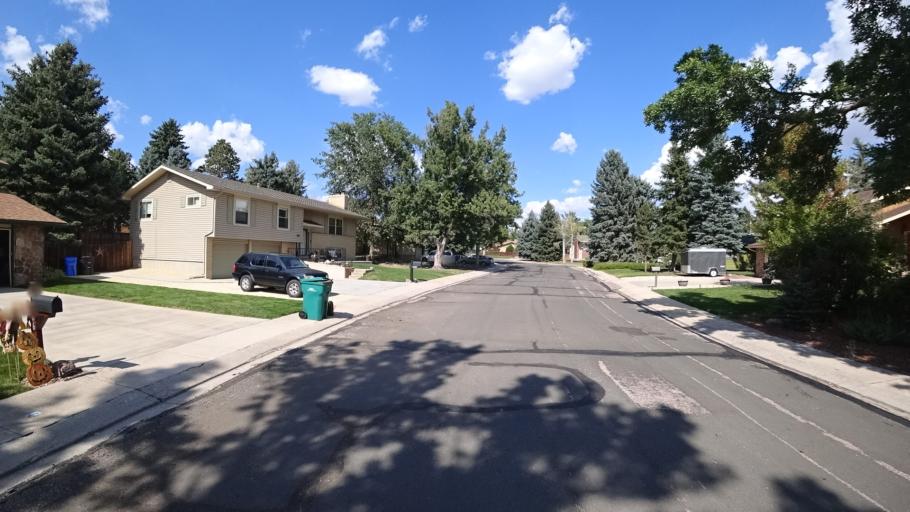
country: US
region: Colorado
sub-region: El Paso County
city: Cimarron Hills
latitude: 38.8768
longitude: -104.7511
